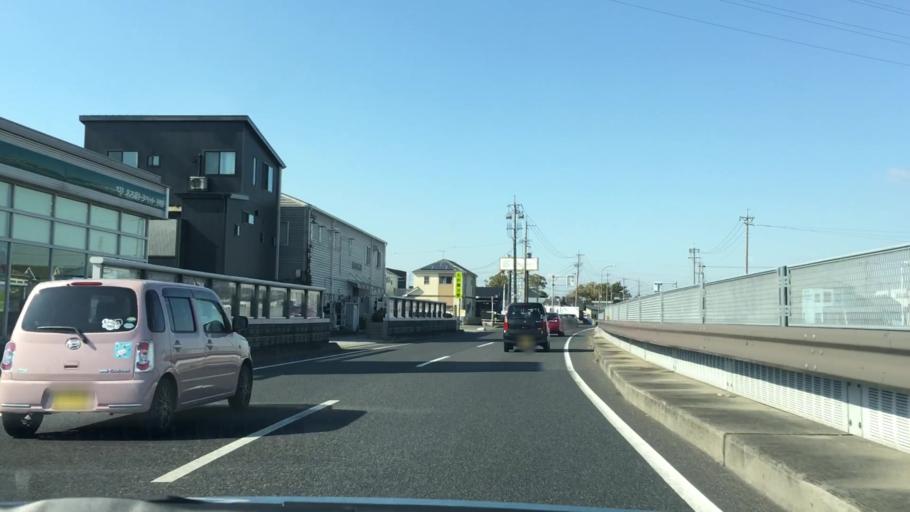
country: JP
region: Aichi
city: Okazaki
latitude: 34.9655
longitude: 137.1352
